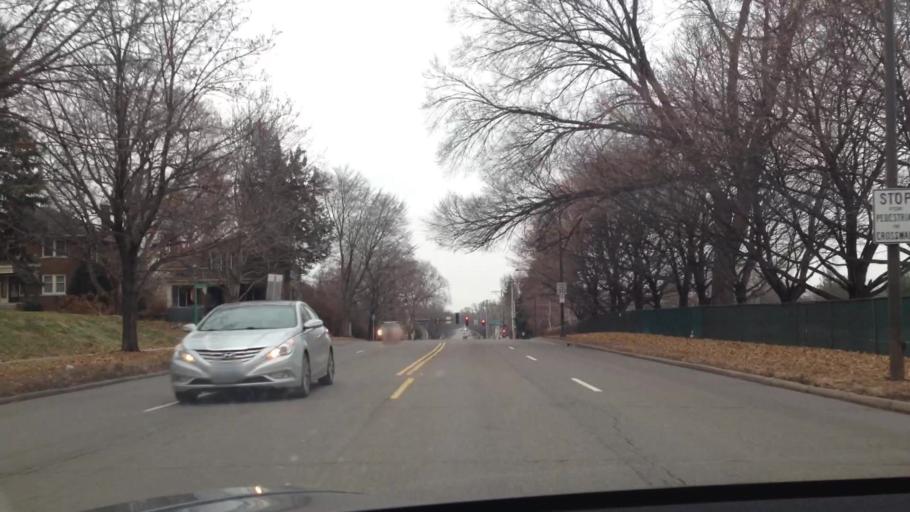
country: US
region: Minnesota
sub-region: Ramsey County
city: Falcon Heights
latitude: 44.9502
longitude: -93.1925
